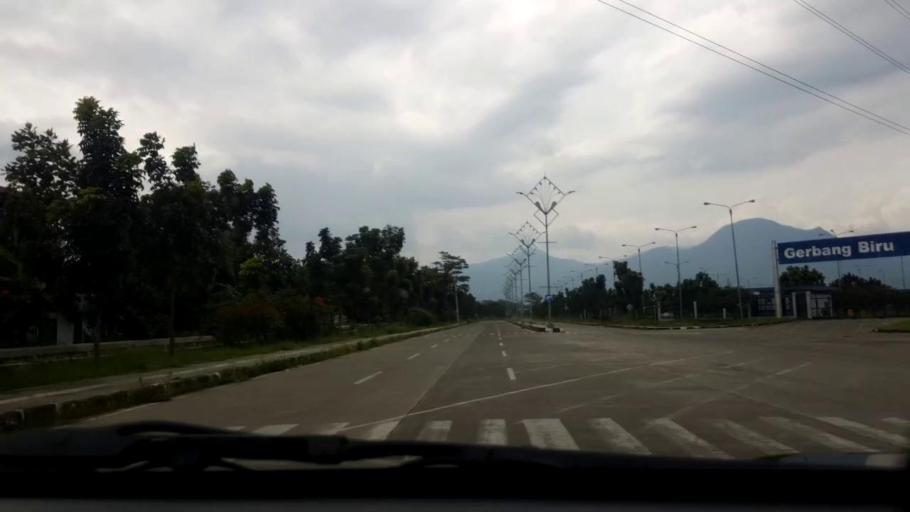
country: ID
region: West Java
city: Cileunyi
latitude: -6.9569
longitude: 107.7106
